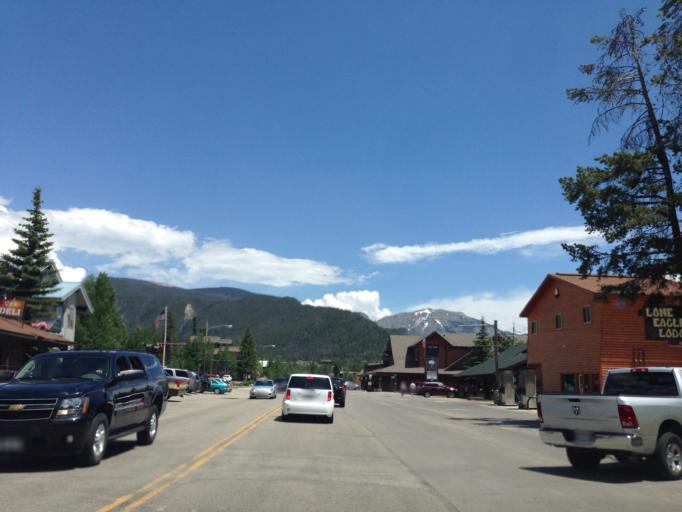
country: US
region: Colorado
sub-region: Grand County
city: Granby
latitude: 40.2525
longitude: -105.8242
